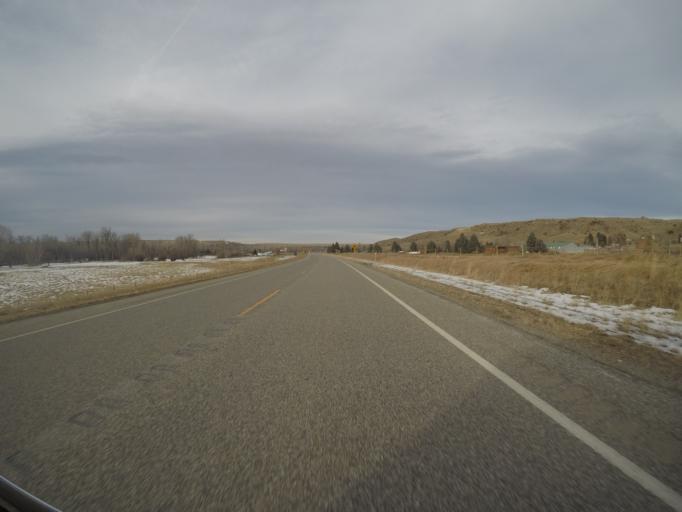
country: US
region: Montana
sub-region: Stillwater County
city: Absarokee
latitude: 45.4771
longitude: -109.4493
